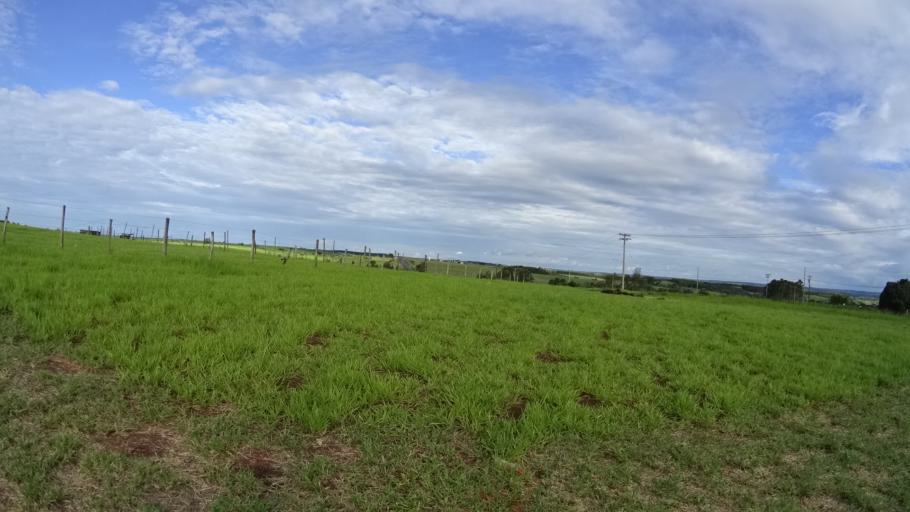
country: BR
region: Sao Paulo
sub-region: Marilia
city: Marilia
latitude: -22.2217
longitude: -49.8797
